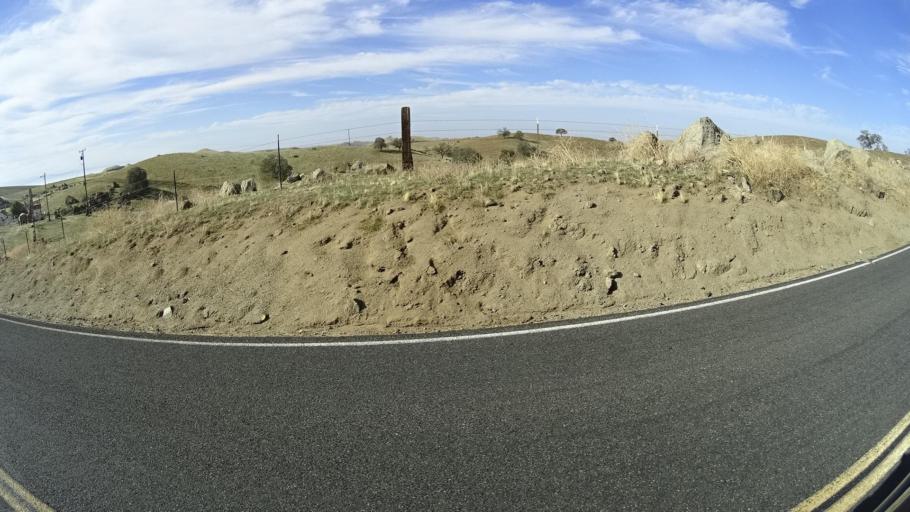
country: US
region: California
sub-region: Kern County
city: Oildale
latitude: 35.6148
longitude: -118.8590
